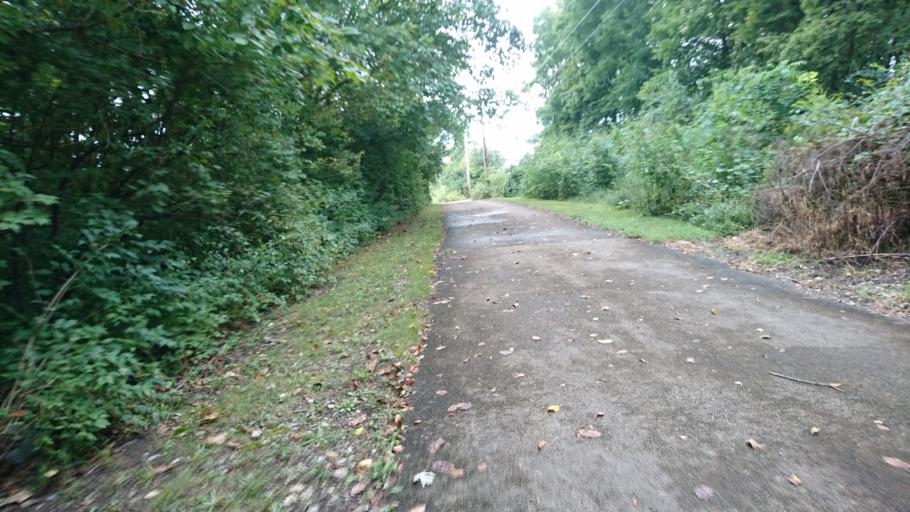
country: US
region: Illinois
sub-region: Sangamon County
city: Southern View
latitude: 39.7577
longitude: -89.6680
